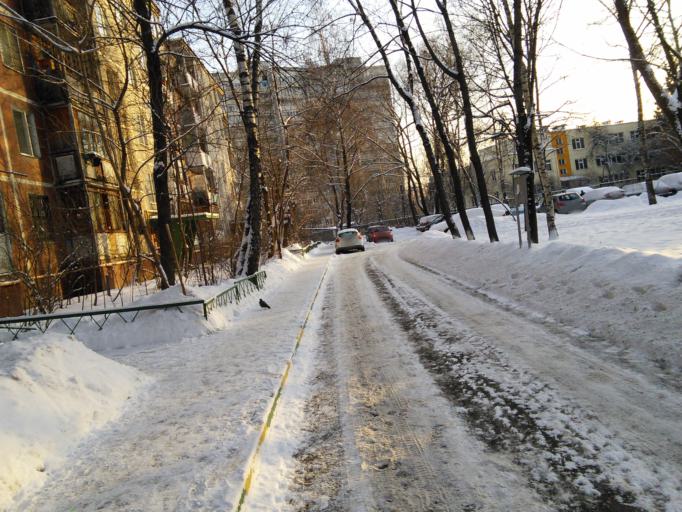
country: RU
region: Moscow
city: Davydkovo
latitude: 55.7242
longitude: 37.4751
